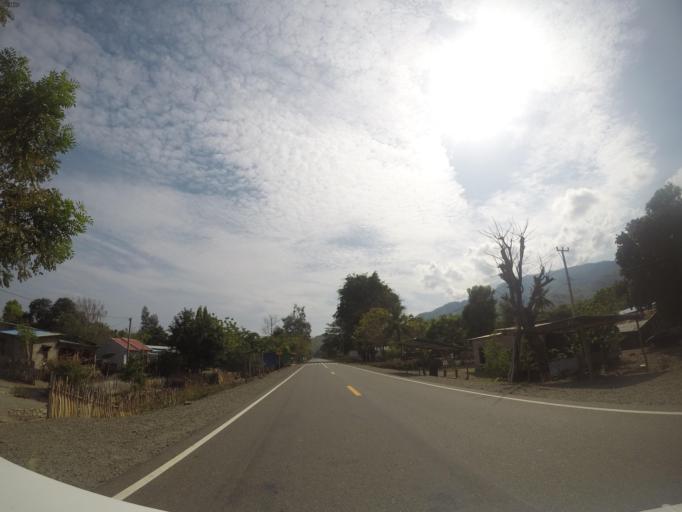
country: ID
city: Metinaro
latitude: -8.4953
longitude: 125.8248
